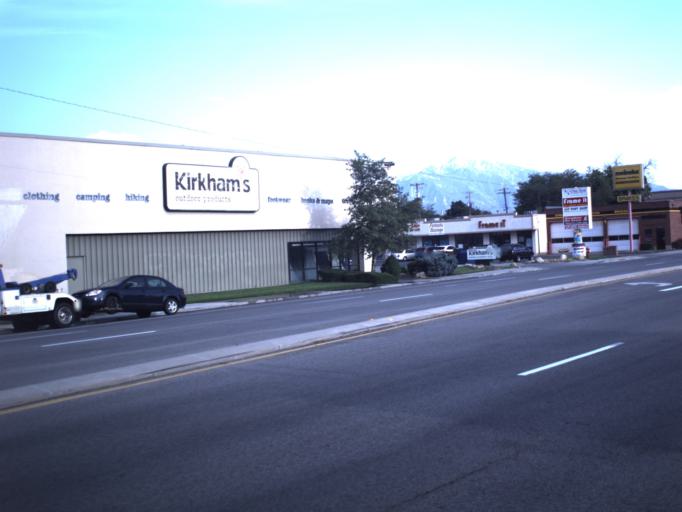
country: US
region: Utah
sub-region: Salt Lake County
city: Centerfield
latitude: 40.7033
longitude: -111.8884
